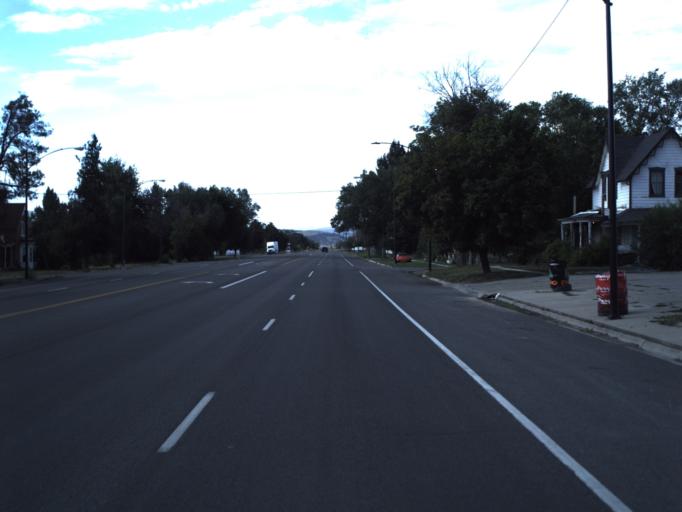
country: US
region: Utah
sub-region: Sanpete County
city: Mount Pleasant
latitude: 39.5504
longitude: -111.4553
